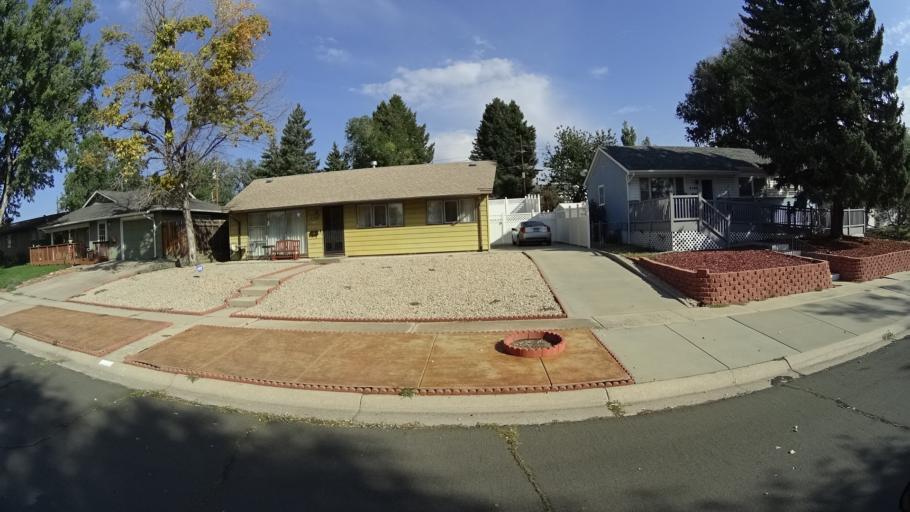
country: US
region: Colorado
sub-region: El Paso County
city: Colorado Springs
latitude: 38.8536
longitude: -104.7722
